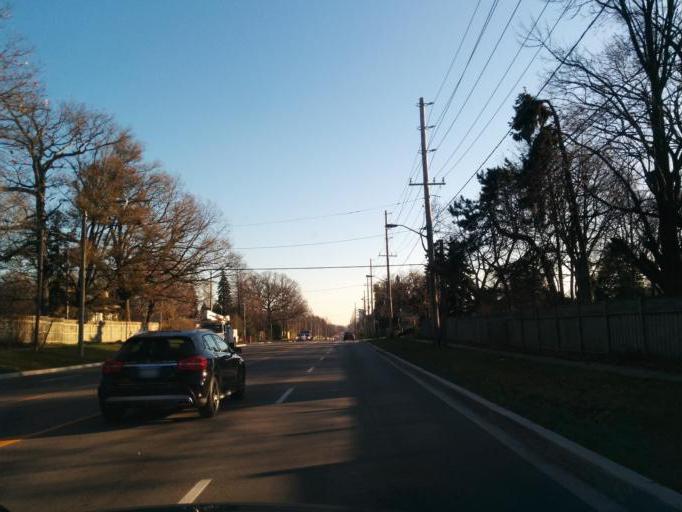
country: CA
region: Ontario
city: Etobicoke
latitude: 43.6686
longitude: -79.5472
